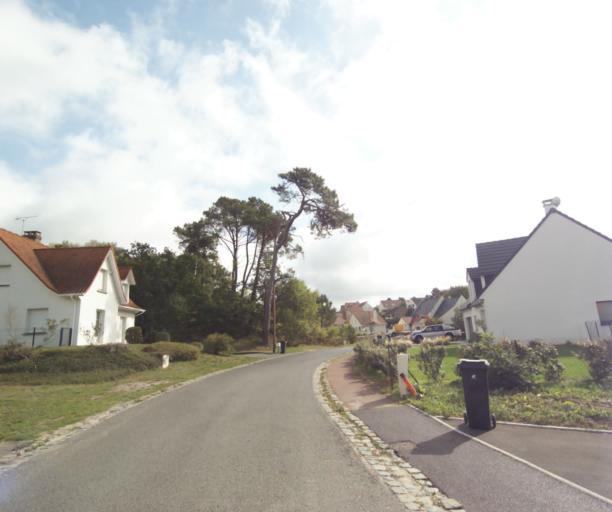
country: FR
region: Nord-Pas-de-Calais
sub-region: Departement du Pas-de-Calais
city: Etaples
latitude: 50.5293
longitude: 1.6343
